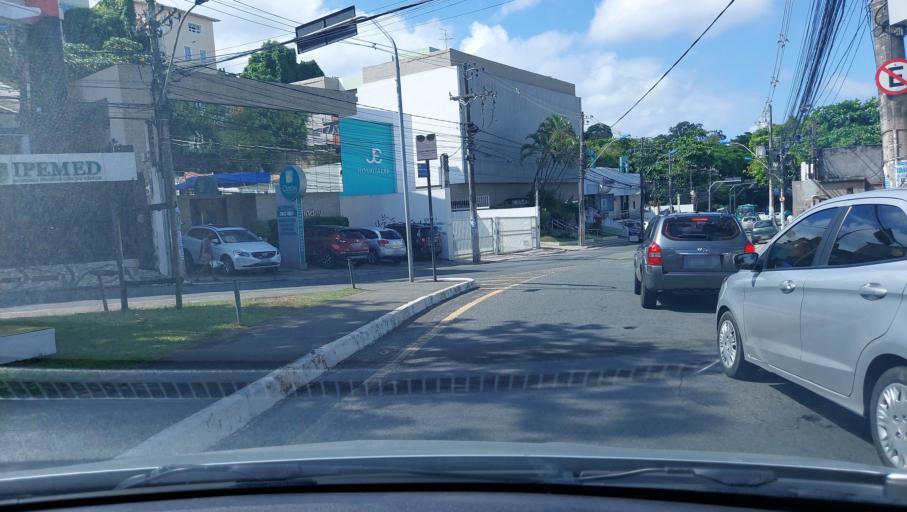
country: BR
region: Bahia
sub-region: Salvador
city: Salvador
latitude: -13.0013
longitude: -38.5055
